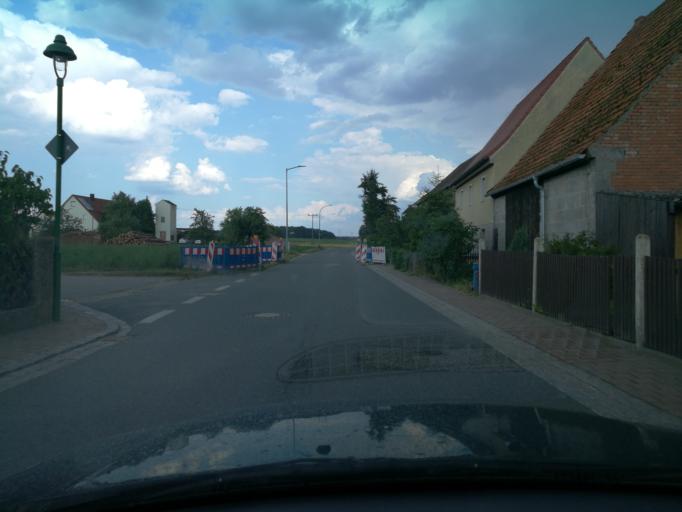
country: DE
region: Bavaria
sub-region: Regierungsbezirk Mittelfranken
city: Langenzenn
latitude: 49.4676
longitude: 10.7793
